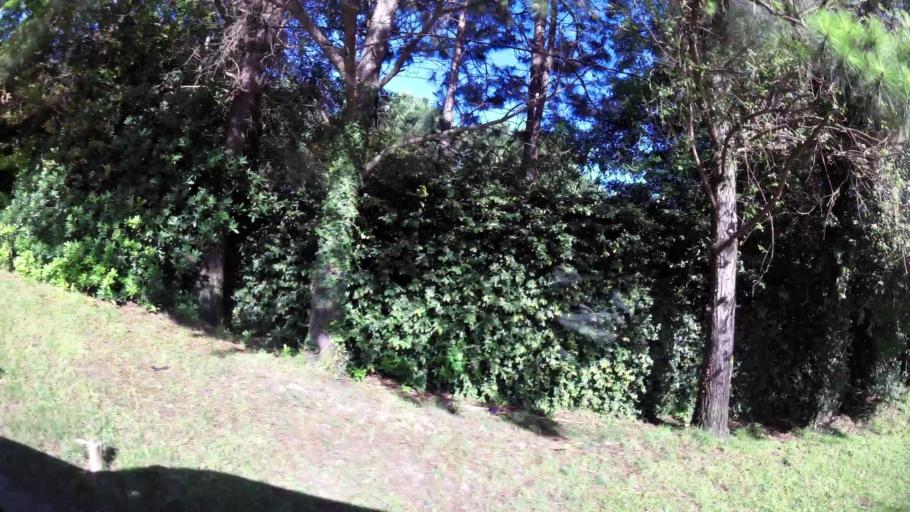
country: UY
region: Canelones
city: Barra de Carrasco
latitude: -34.8647
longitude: -56.0306
